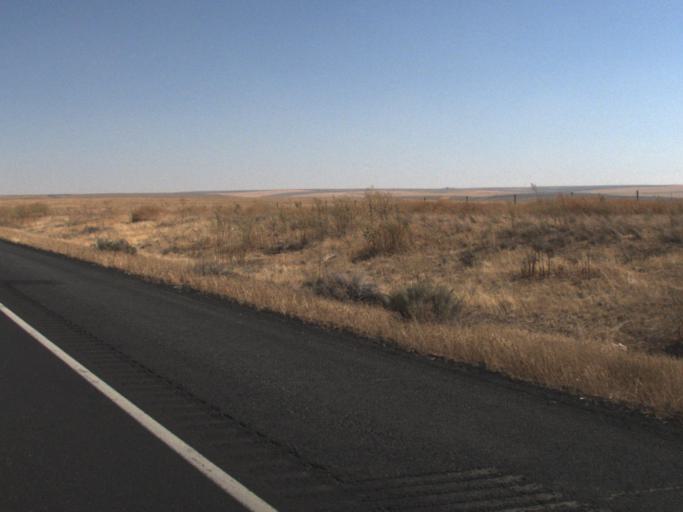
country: US
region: Washington
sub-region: Grant County
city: Warden
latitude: 47.0859
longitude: -118.7830
